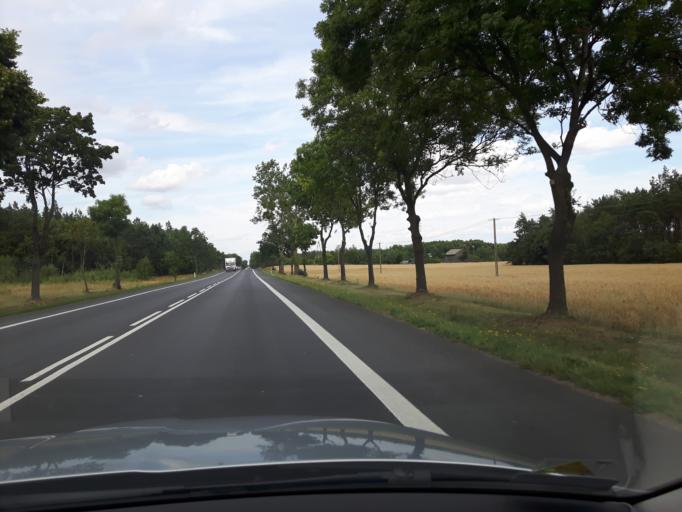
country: PL
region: Masovian Voivodeship
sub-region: Powiat mlawski
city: Strzegowo
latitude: 52.9704
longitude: 20.3083
